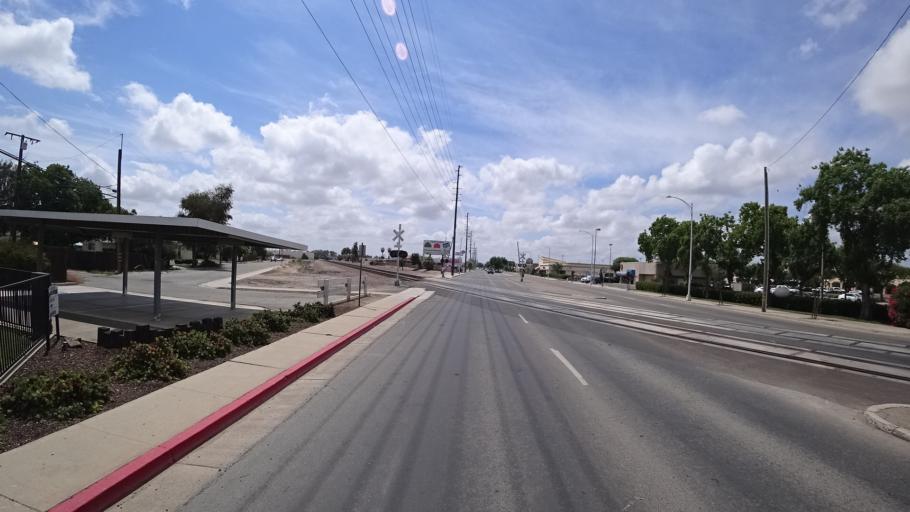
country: US
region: California
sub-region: Kings County
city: Hanford
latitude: 36.3318
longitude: -119.6551
